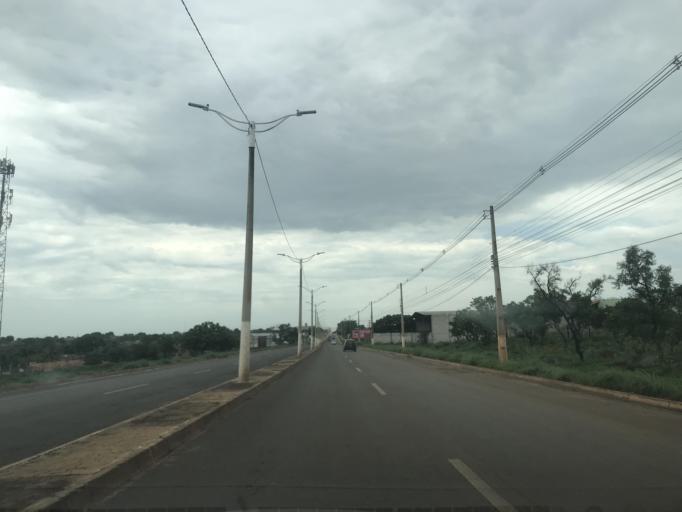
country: BR
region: Goias
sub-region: Luziania
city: Luziania
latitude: -16.2180
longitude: -47.9328
